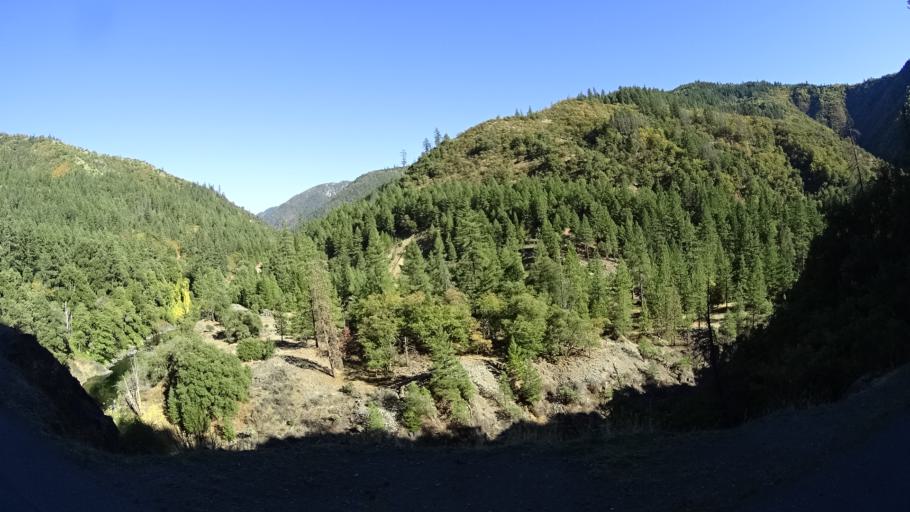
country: US
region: California
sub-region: Humboldt County
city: Willow Creek
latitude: 41.2702
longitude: -123.3057
